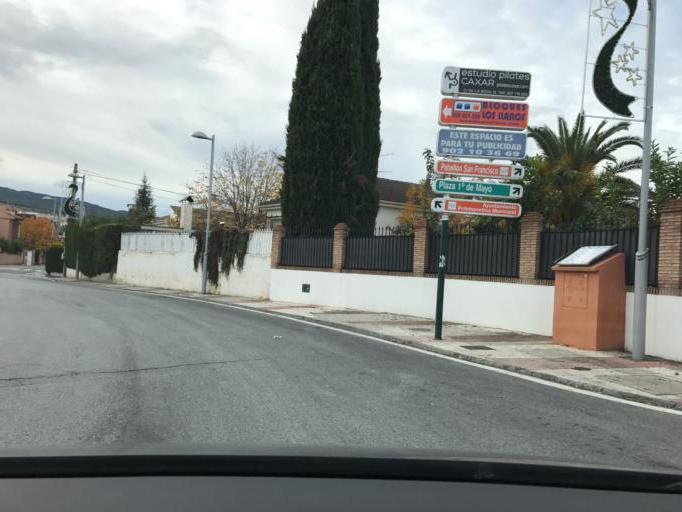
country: ES
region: Andalusia
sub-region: Provincia de Granada
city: Cajar
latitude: 37.1390
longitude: -3.5708
